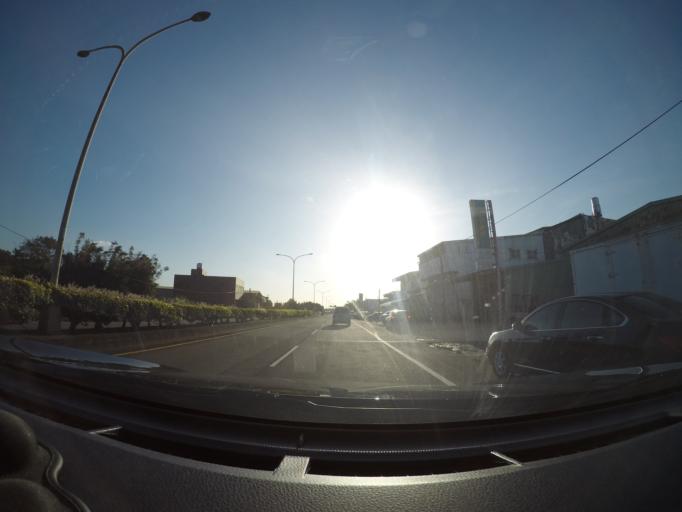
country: TW
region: Taiwan
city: Taoyuan City
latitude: 25.0778
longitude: 121.2068
